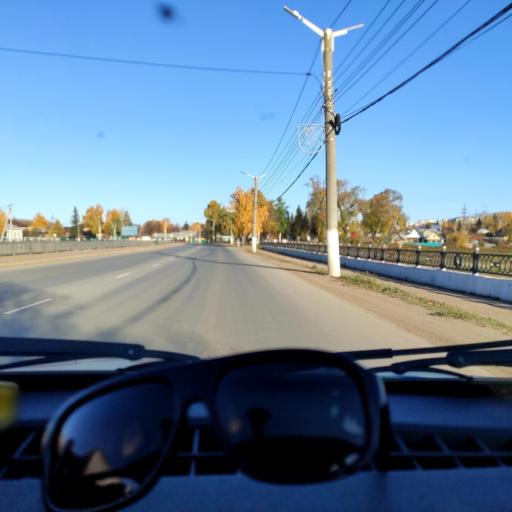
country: RU
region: Bashkortostan
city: Blagoveshchensk
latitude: 55.0328
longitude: 55.9680
